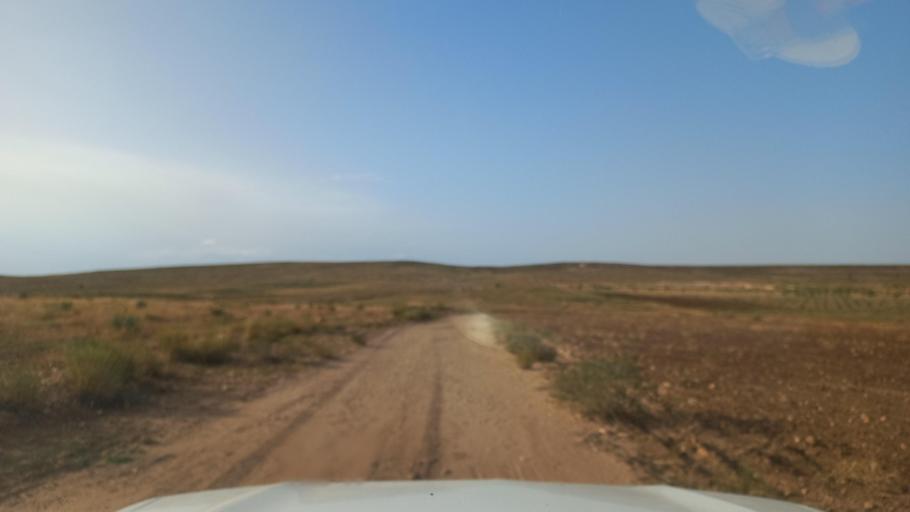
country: TN
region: Al Qasrayn
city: Kasserine
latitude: 35.3557
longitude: 8.8417
